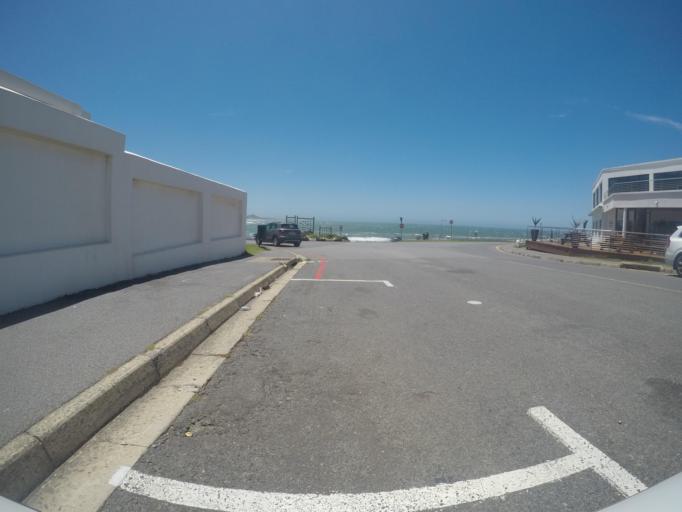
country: ZA
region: Eastern Cape
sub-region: Buffalo City Metropolitan Municipality
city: East London
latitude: -32.9391
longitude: 28.0320
